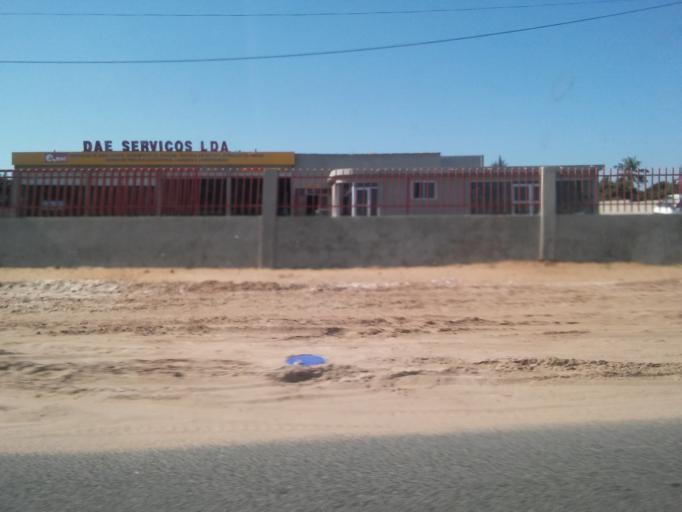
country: MZ
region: Maputo City
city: Maputo
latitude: -25.8624
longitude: 32.5666
